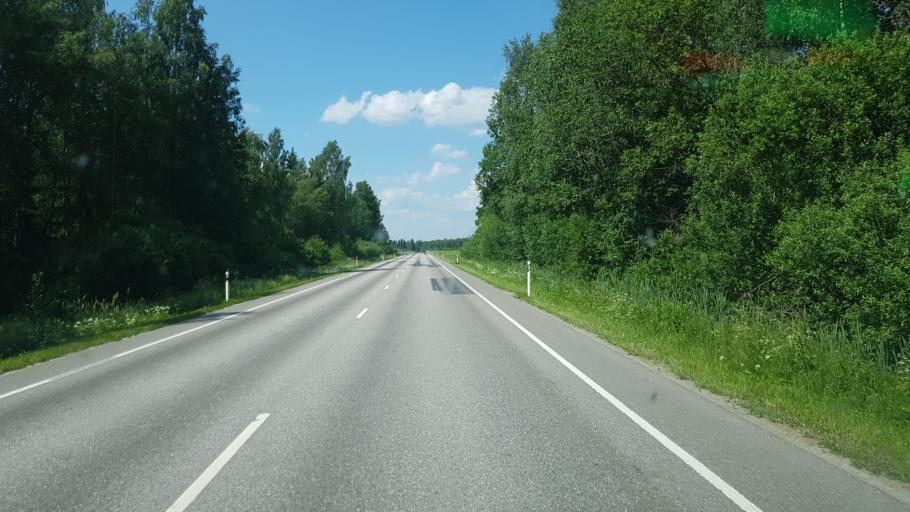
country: EE
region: Jogevamaa
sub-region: Tabivere vald
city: Tabivere
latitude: 58.6071
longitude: 26.5841
